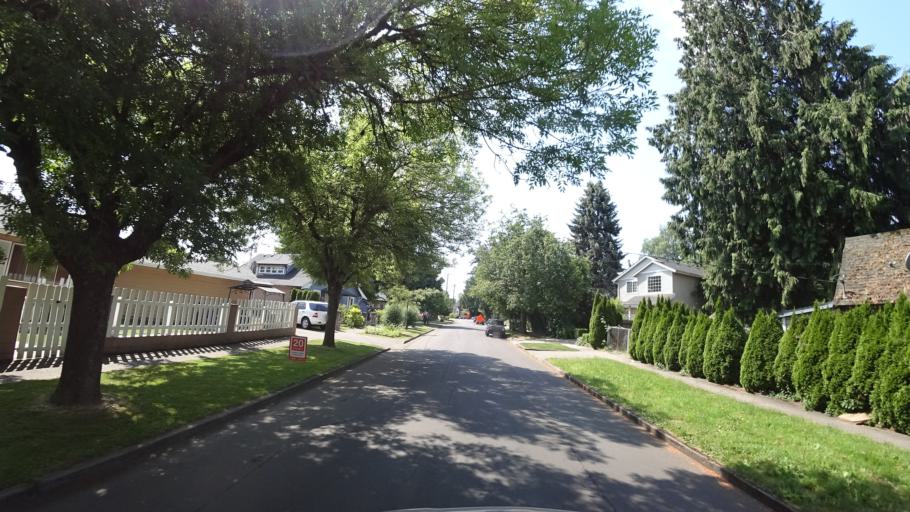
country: US
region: Oregon
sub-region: Washington County
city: West Haven
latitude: 45.5980
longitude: -122.7490
